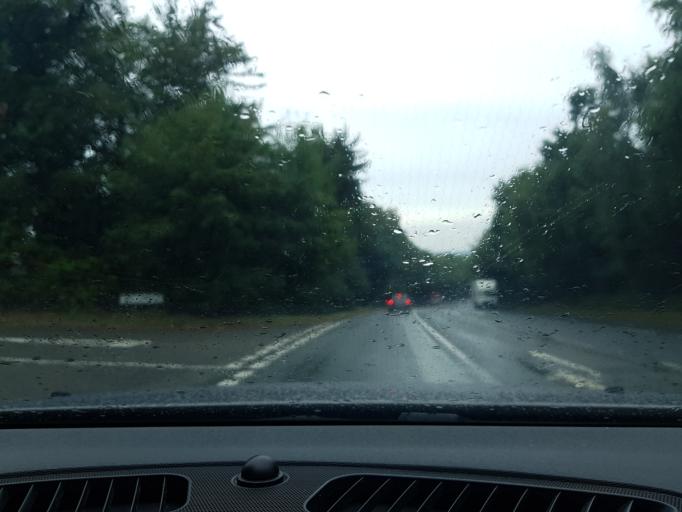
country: GB
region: England
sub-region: Surrey
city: Farnham
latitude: 51.2379
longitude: -0.8363
